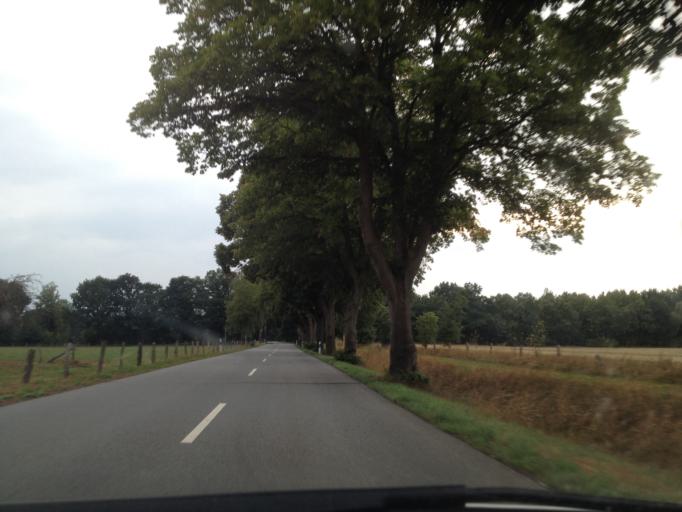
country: DE
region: Schleswig-Holstein
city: Rickling
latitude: 54.0067
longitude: 10.1981
